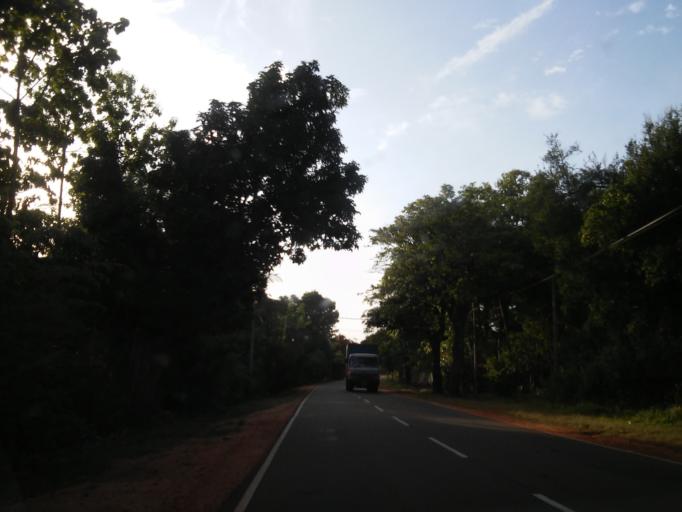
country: LK
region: Central
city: Sigiriya
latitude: 8.0950
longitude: 80.6192
